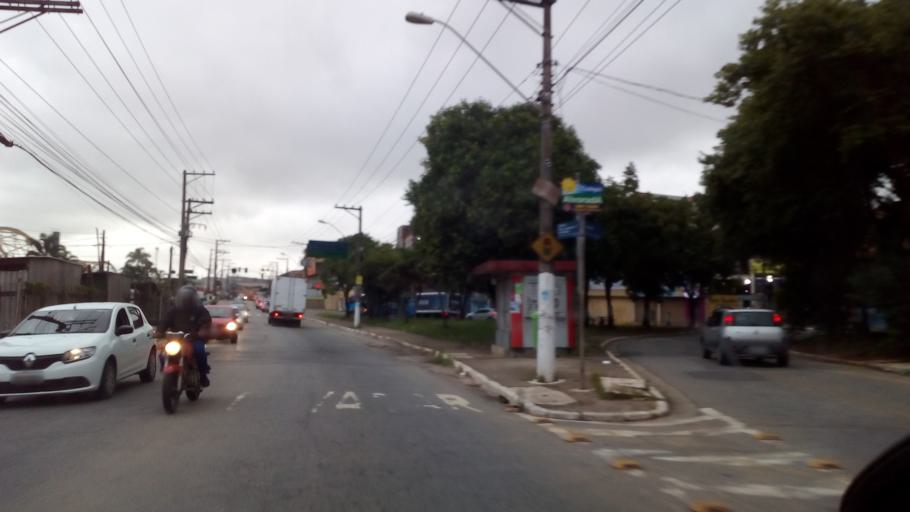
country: BR
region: Sao Paulo
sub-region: Itaquaquecetuba
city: Itaquaquecetuba
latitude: -23.4362
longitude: -46.4061
